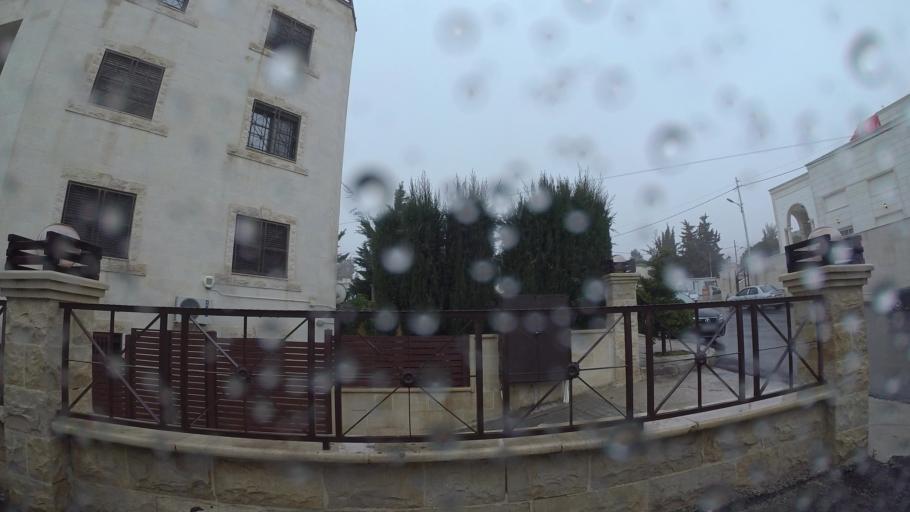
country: JO
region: Amman
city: Al Jubayhah
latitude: 32.0014
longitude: 35.8233
